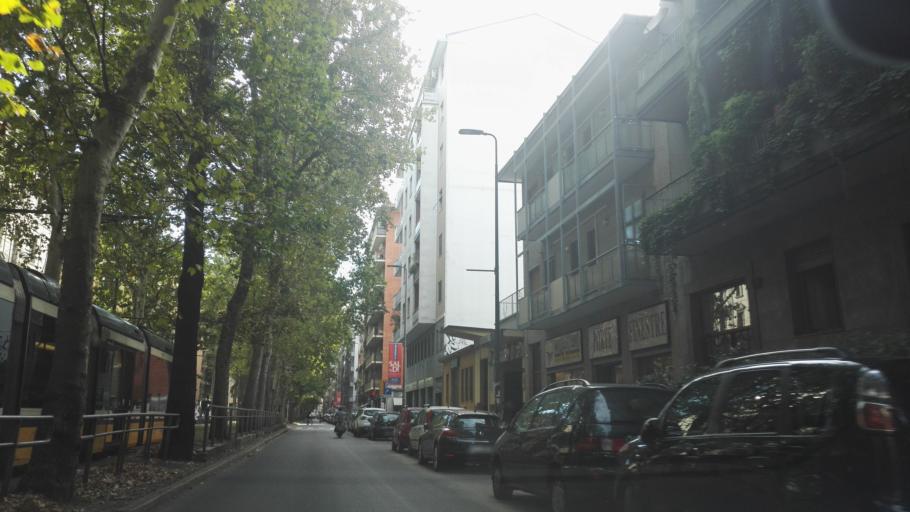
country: IT
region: Lombardy
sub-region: Citta metropolitana di Milano
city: Romano Banco
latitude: 45.4518
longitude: 9.1518
